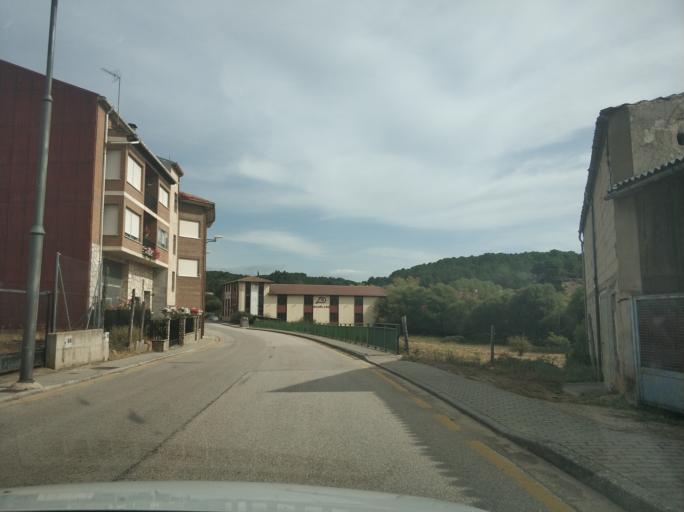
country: ES
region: Castille and Leon
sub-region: Provincia de Soria
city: Navaleno
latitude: 41.8385
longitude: -3.0024
